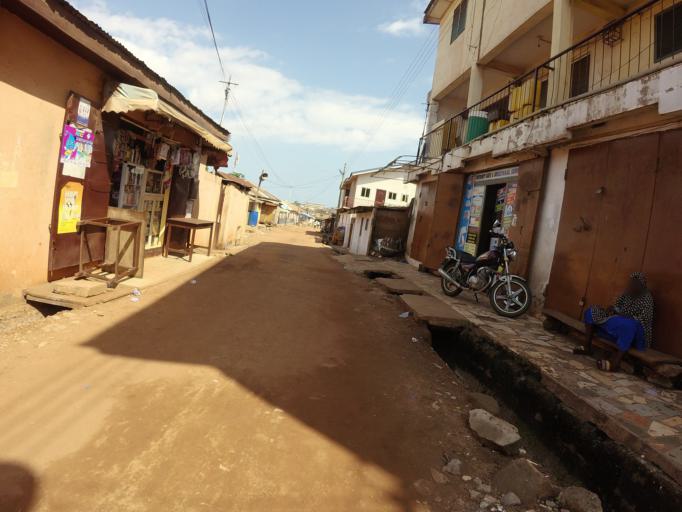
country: GH
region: Greater Accra
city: Accra
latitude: 5.5858
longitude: -0.2055
